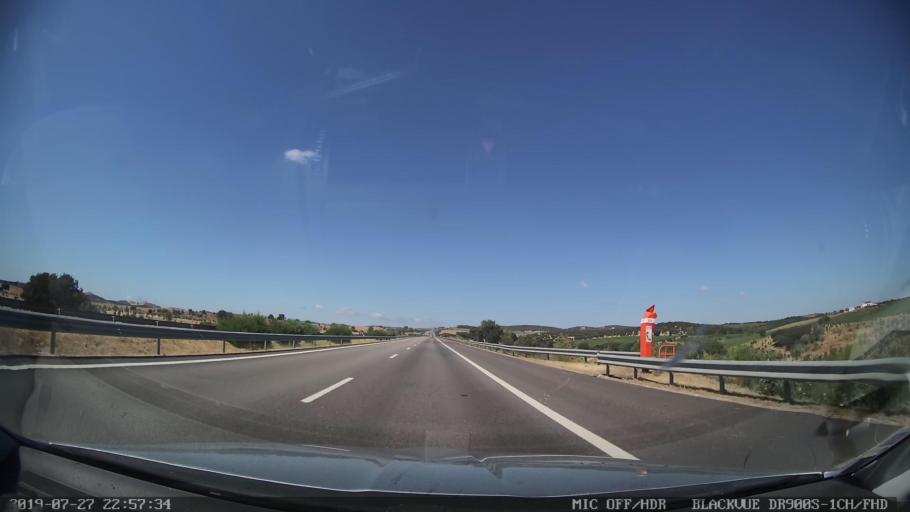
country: PT
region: Evora
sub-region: Borba
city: Borba
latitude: 38.8319
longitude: -7.4219
